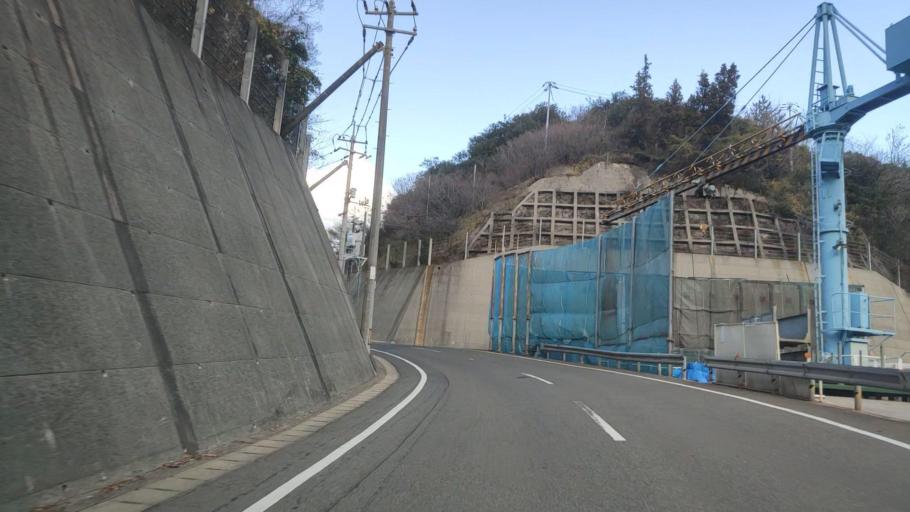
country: JP
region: Hiroshima
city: Innoshima
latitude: 34.2081
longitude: 133.1216
